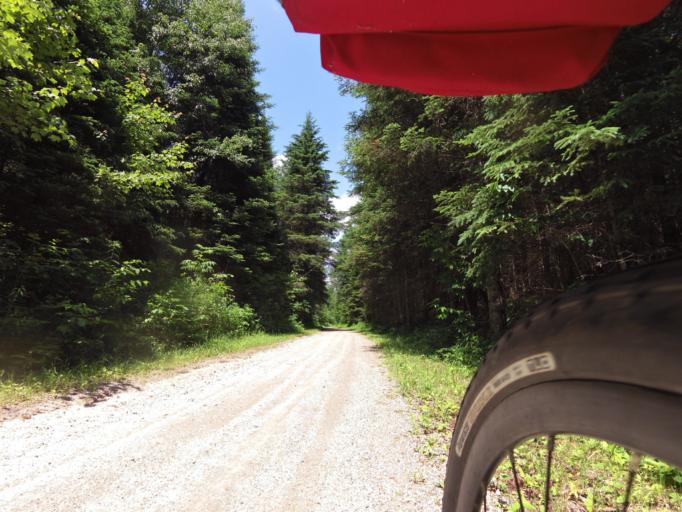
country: CA
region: Quebec
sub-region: Outaouais
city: Maniwaki
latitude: 46.0845
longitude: -76.0677
